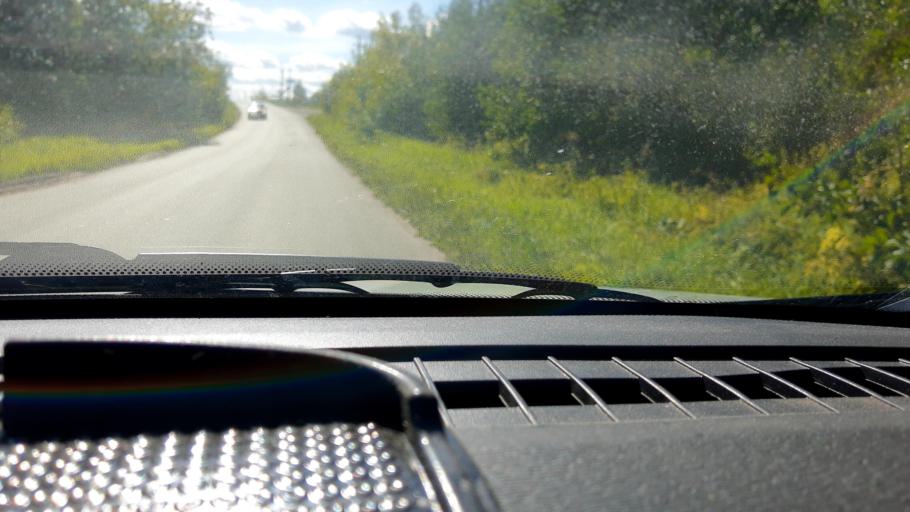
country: RU
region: Nizjnij Novgorod
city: Lukino
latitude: 56.4217
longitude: 43.6512
